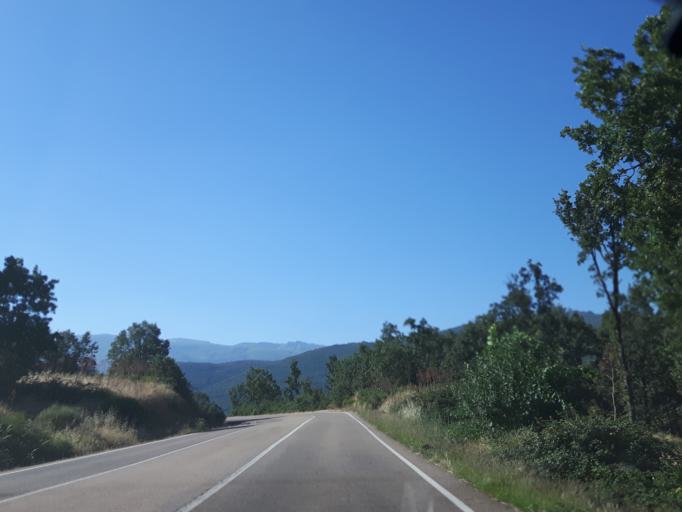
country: ES
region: Castille and Leon
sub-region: Provincia de Salamanca
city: Navalmoral de Bejar
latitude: 40.4042
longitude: -5.7945
